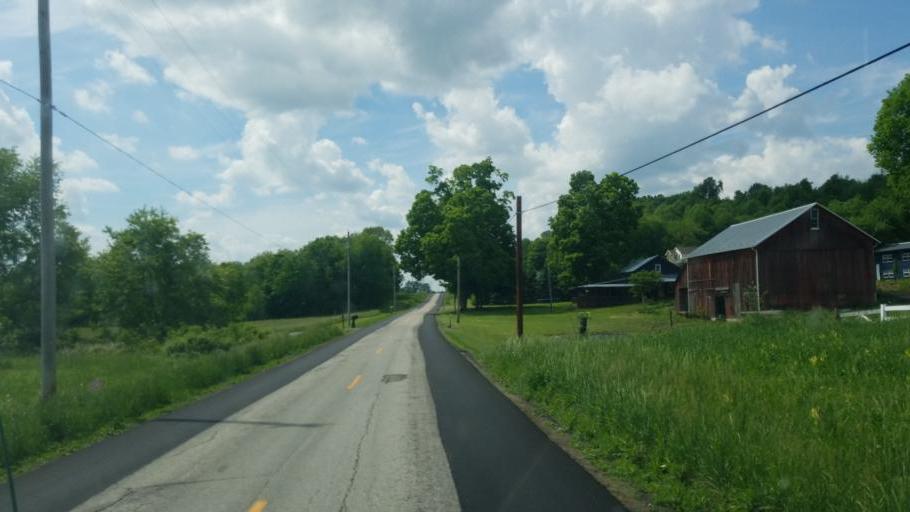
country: US
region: Ohio
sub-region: Sandusky County
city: Bellville
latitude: 40.6653
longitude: -82.4222
